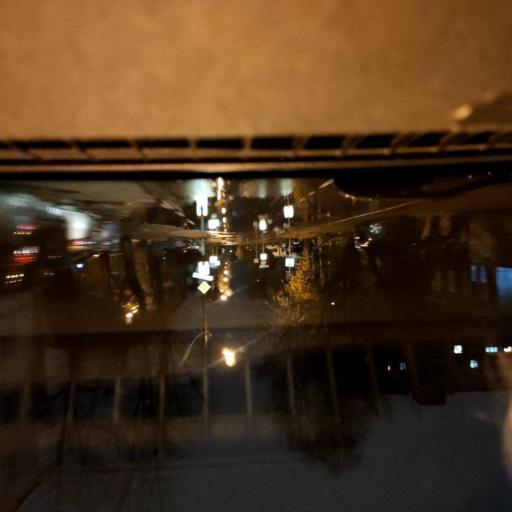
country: RU
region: Perm
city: Perm
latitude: 58.0107
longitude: 56.2027
